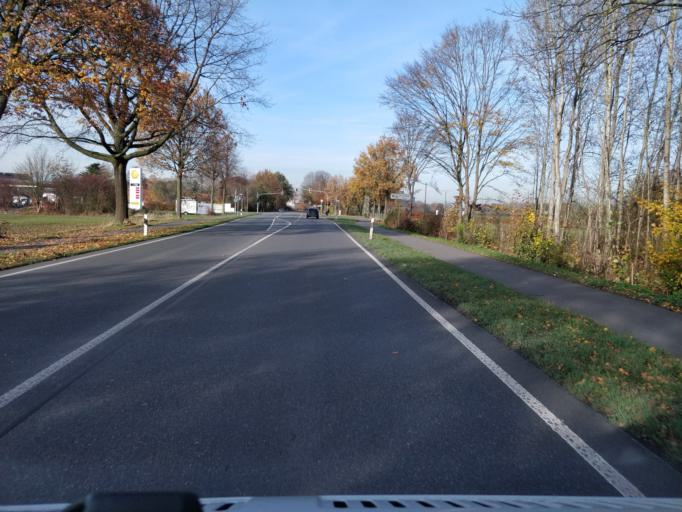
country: DE
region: North Rhine-Westphalia
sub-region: Regierungsbezirk Dusseldorf
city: Hamminkeln
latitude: 51.7405
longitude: 6.5955
